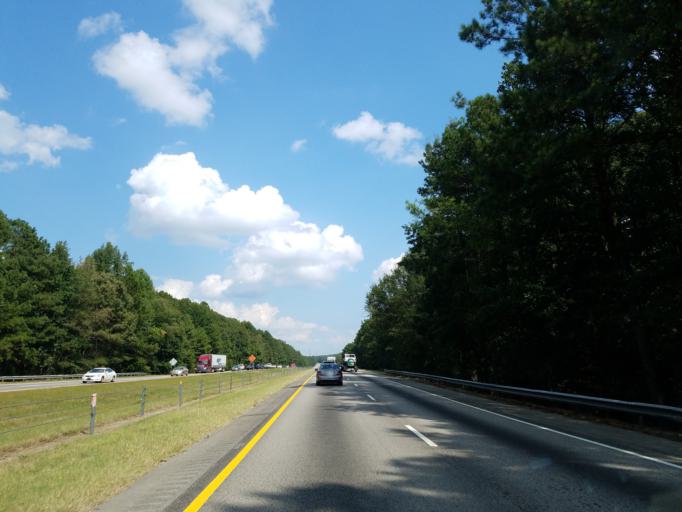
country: US
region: Georgia
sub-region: Barrow County
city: Auburn
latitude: 34.0847
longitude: -83.8630
